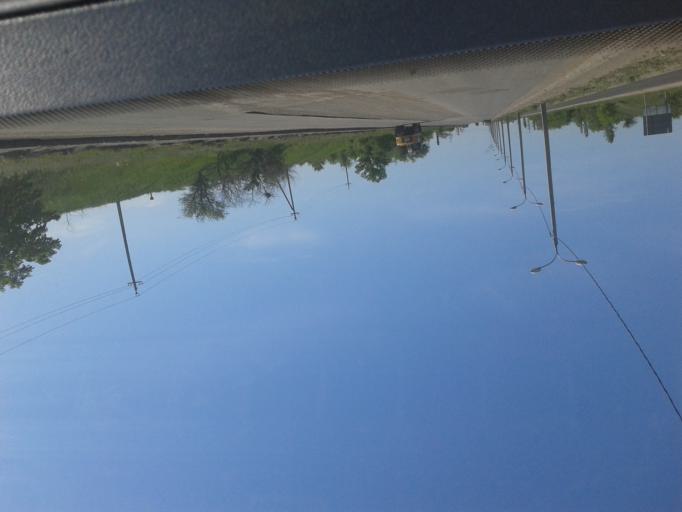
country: RU
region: Volgograd
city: Volgograd
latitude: 48.7374
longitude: 44.4588
